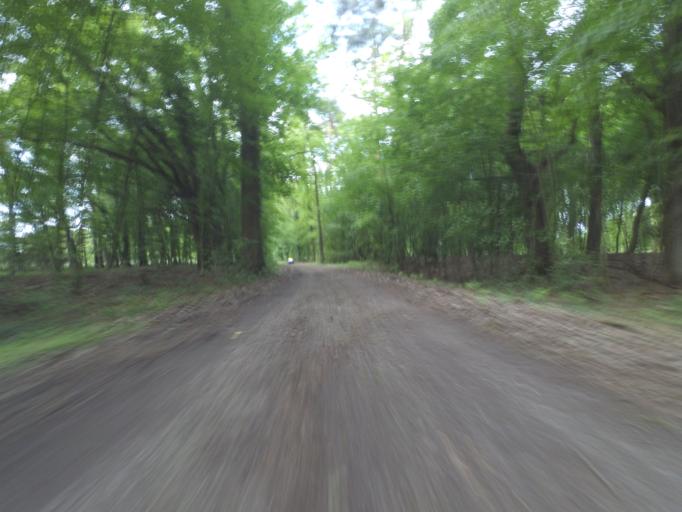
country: DE
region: Lower Saxony
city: Wietze
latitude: 52.6839
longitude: 9.8382
